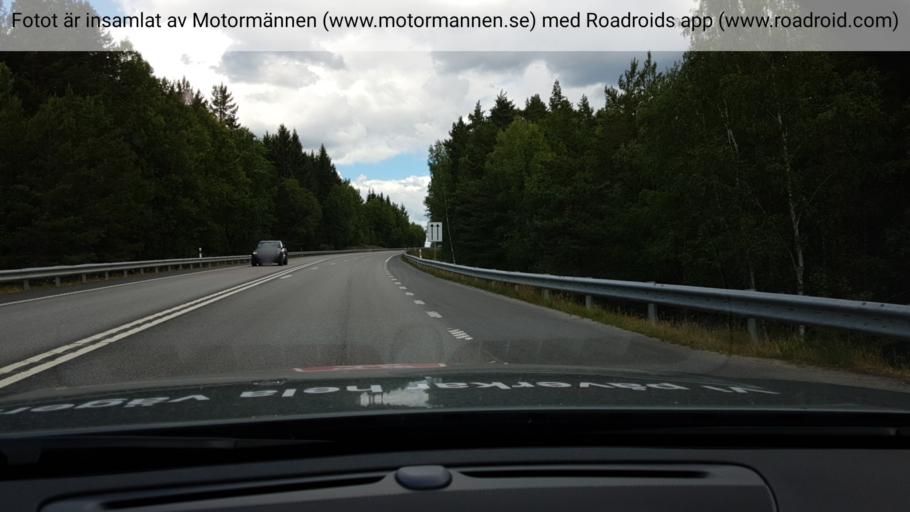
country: SE
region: Stockholm
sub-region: Lidingo
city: Brevik
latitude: 59.4345
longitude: 18.2193
